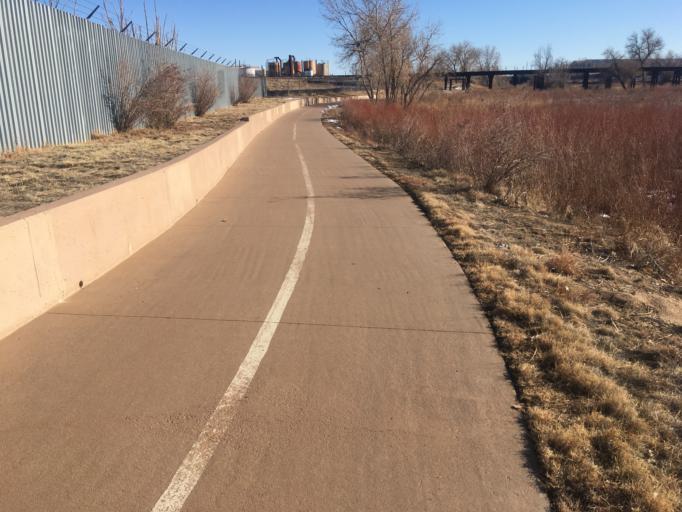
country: US
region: Colorado
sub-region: Adams County
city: Commerce City
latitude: 39.8019
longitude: -104.9395
